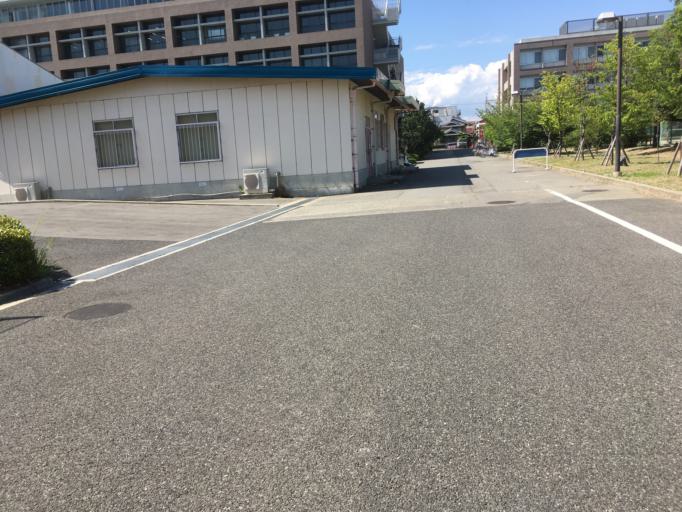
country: JP
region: Osaka
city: Sakai
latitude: 34.5927
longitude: 135.5083
